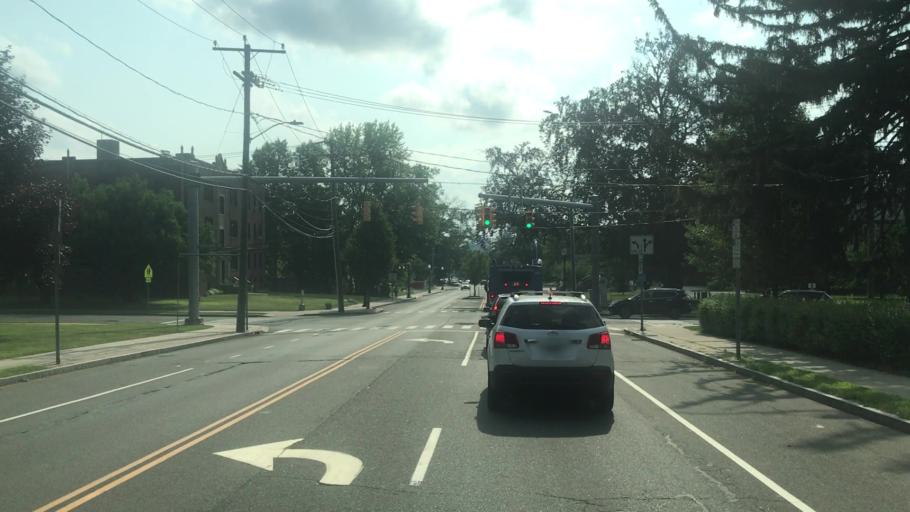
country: US
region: Connecticut
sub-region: Hartford County
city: West Hartford
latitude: 41.7654
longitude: -72.7187
